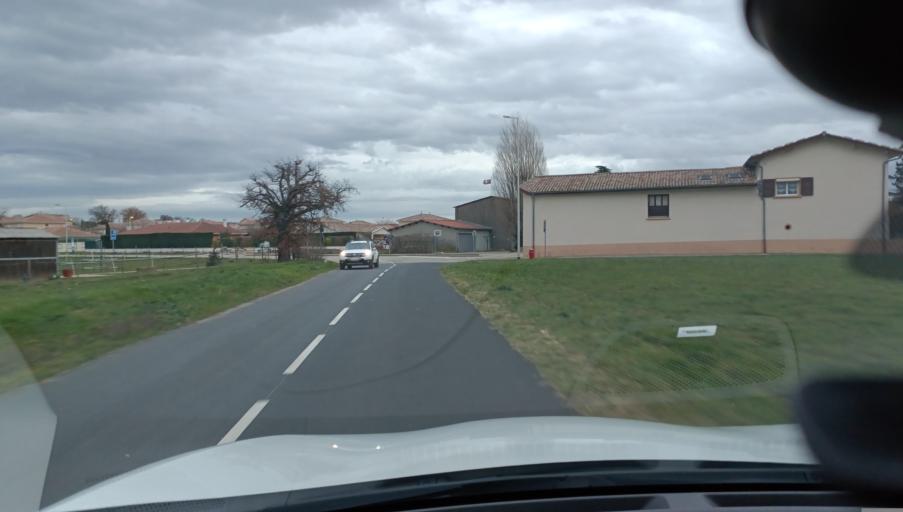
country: FR
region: Rhone-Alpes
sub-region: Departement de l'Isere
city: Chasse-sur-Rhone
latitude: 45.5787
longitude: 4.8267
